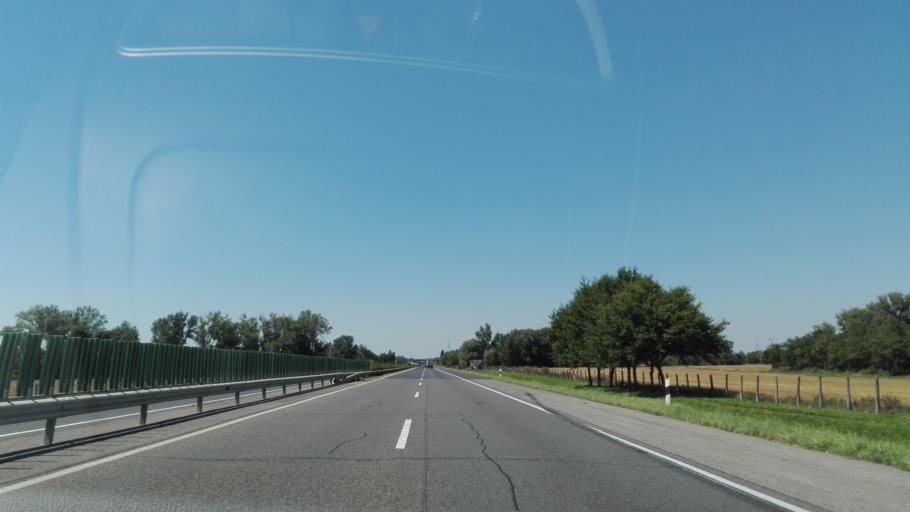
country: HU
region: Gyor-Moson-Sopron
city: Lebeny
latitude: 47.7684
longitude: 17.3793
